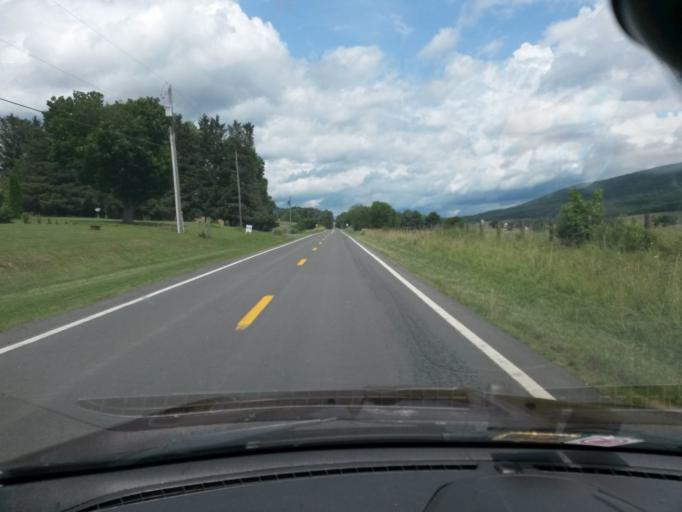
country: US
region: West Virginia
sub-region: Monroe County
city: Union
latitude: 37.5677
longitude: -80.3614
